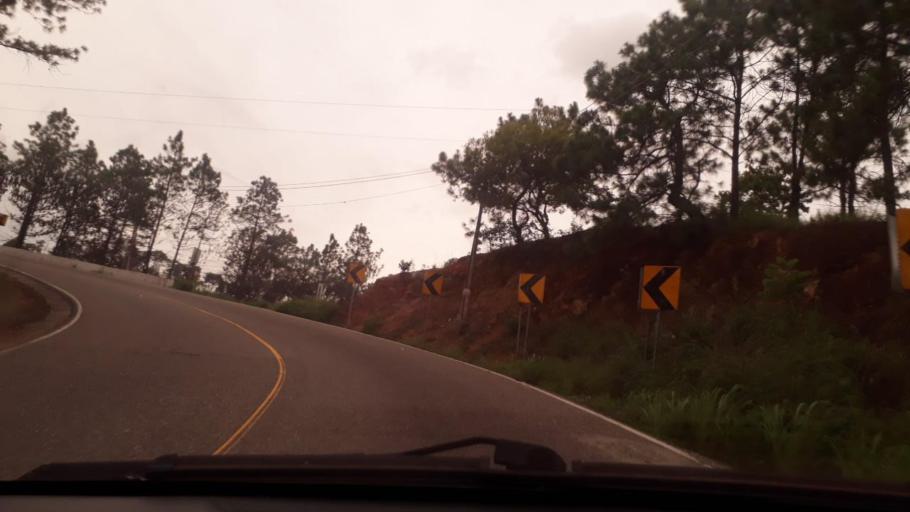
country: GT
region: Chiquimula
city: San Jose La Arada
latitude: 14.7098
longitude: -89.6272
